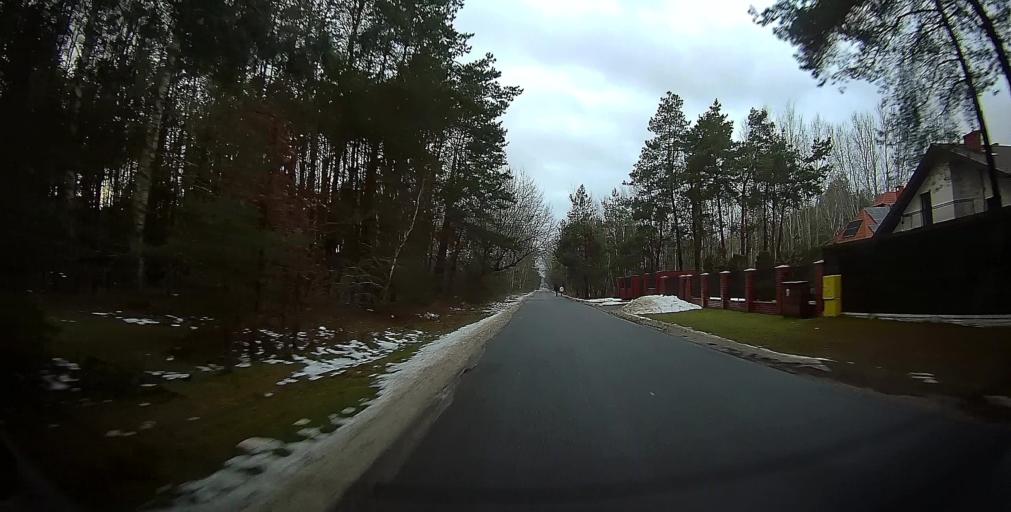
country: PL
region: Masovian Voivodeship
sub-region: Radom
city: Radom
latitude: 51.4511
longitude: 21.1321
